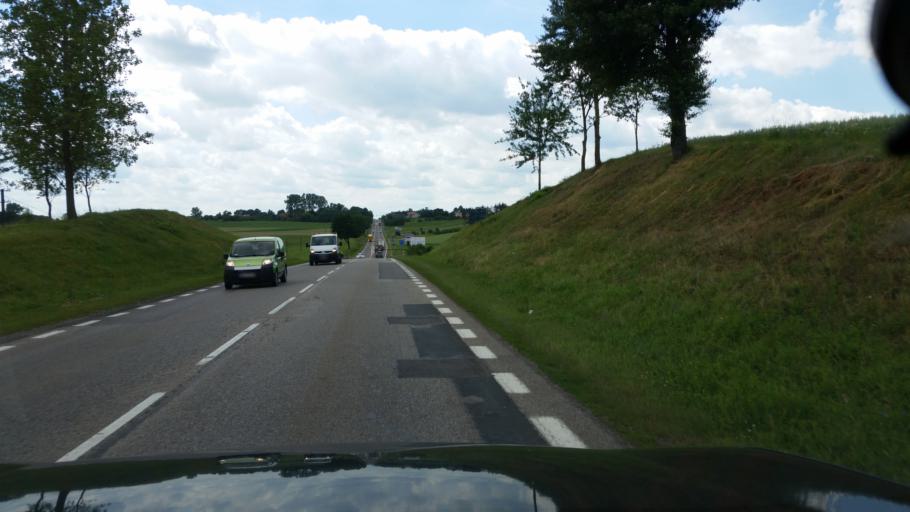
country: PL
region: Podlasie
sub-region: Powiat lomzynski
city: Piatnica
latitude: 53.2390
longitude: 22.1156
